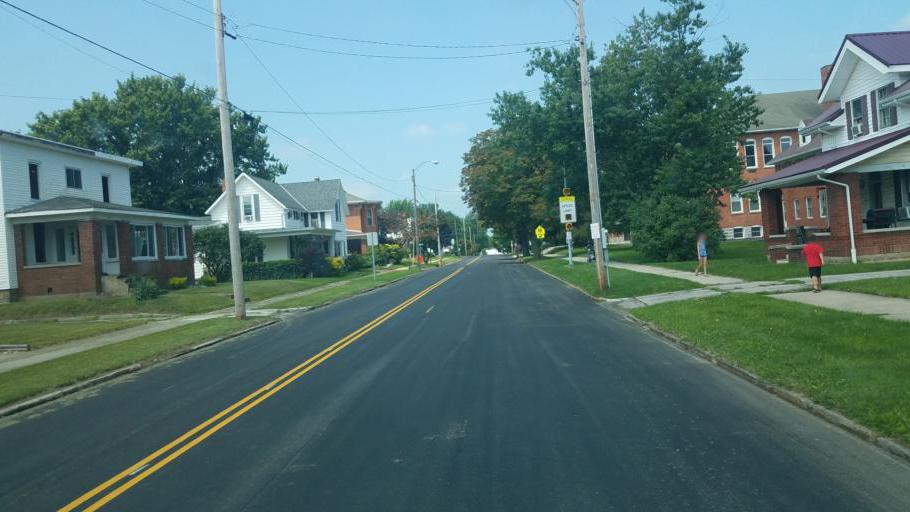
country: US
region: Ohio
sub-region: Huron County
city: Willard
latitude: 40.9623
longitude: -82.8563
